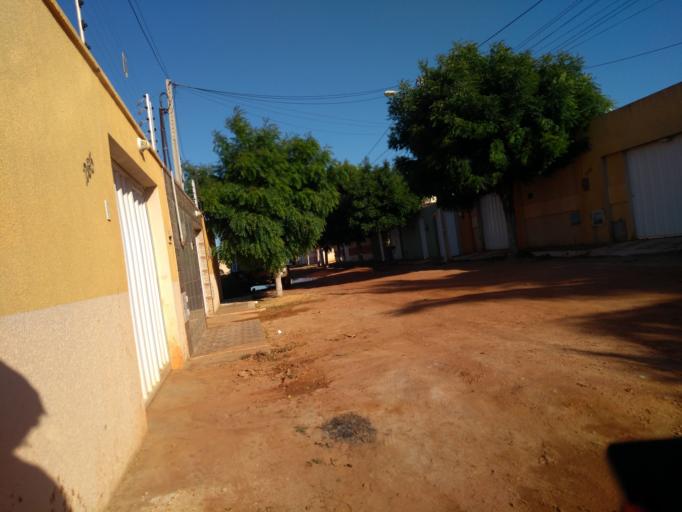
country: BR
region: Ceara
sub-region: Aracati
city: Aracati
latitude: -4.5714
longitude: -37.7964
